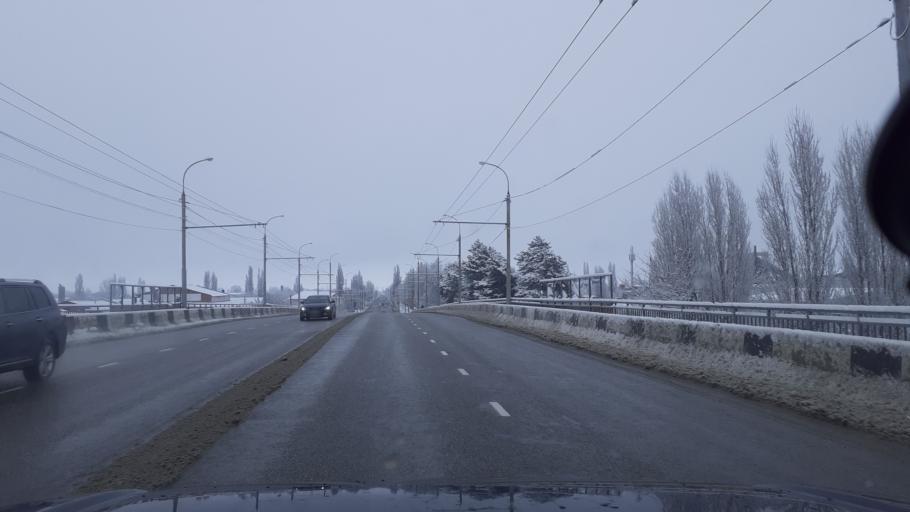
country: RU
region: Adygeya
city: Maykop
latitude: 44.6215
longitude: 40.1219
